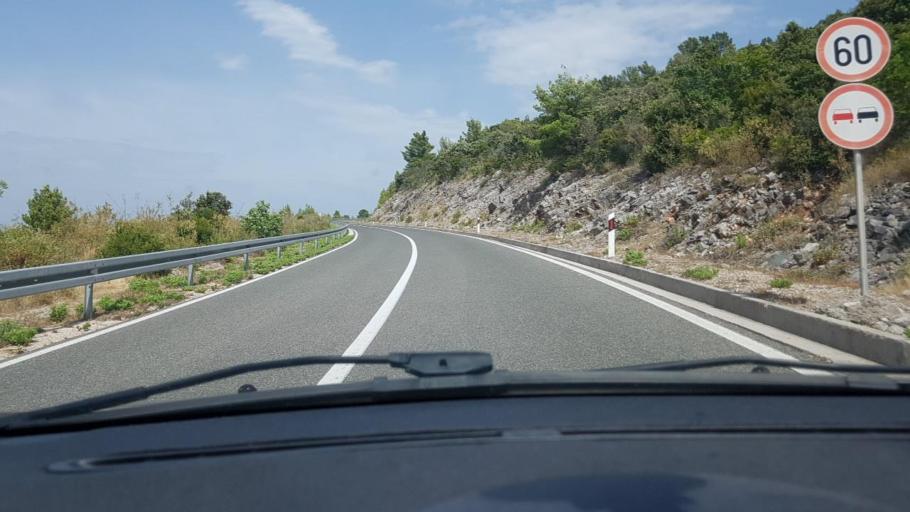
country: HR
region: Dubrovacko-Neretvanska
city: Smokvica
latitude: 42.9559
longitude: 16.9357
